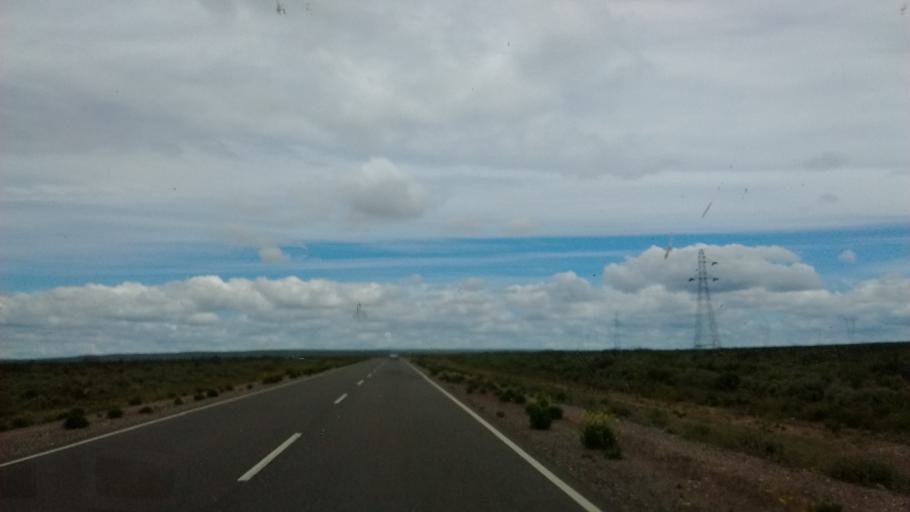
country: AR
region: Neuquen
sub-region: Departamento de Picun Leufu
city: Picun Leufu
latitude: -39.6994
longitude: -69.4927
